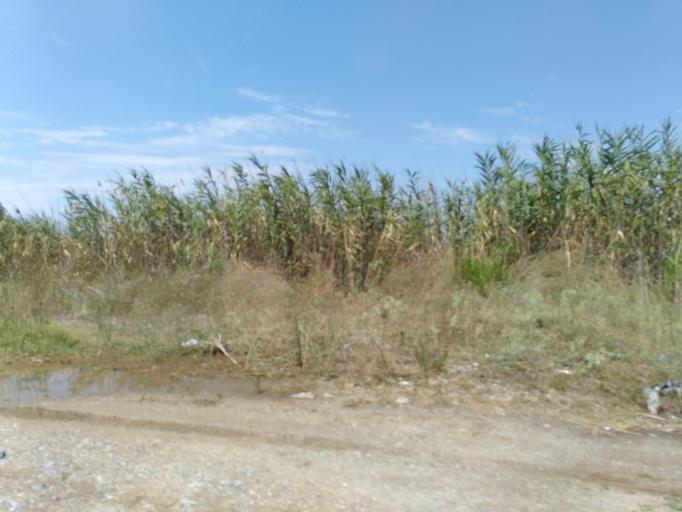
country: GR
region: Central Macedonia
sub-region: Nomos Thessalonikis
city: Nea Michaniona
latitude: 40.4349
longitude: 22.8687
